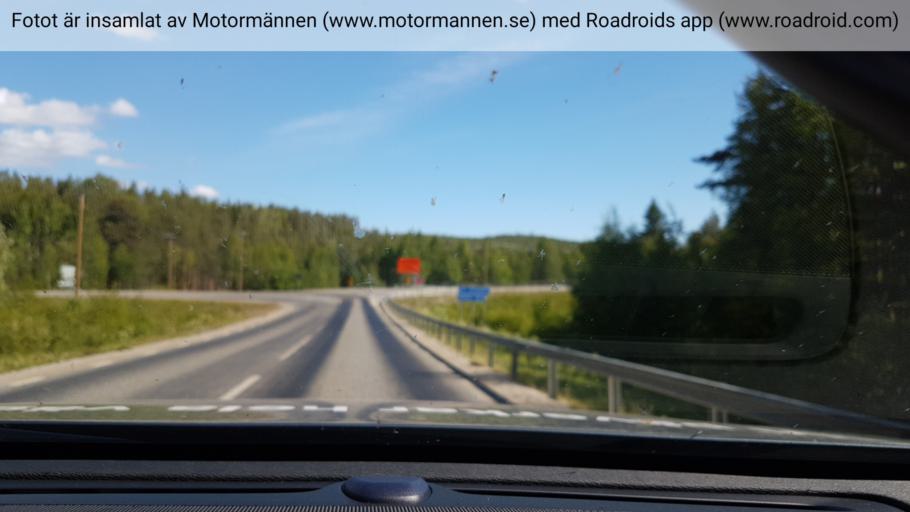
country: SE
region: Vaesterbotten
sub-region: Lycksele Kommun
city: Lycksele
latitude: 64.5764
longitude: 18.6507
